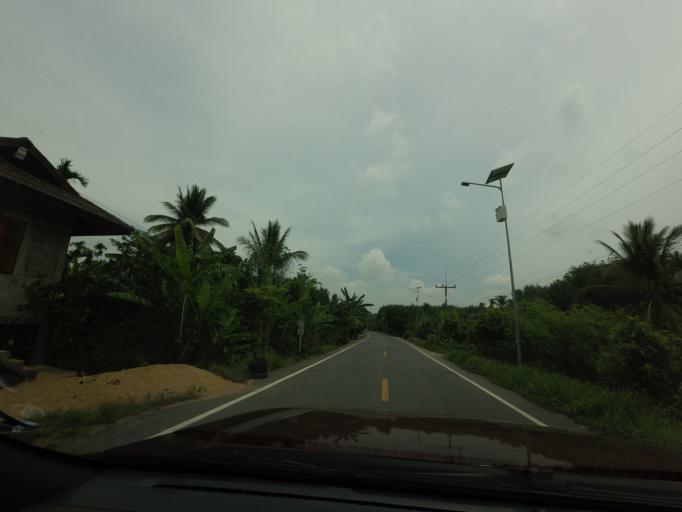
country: TH
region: Pattani
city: Yarang
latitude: 6.7137
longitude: 101.2981
